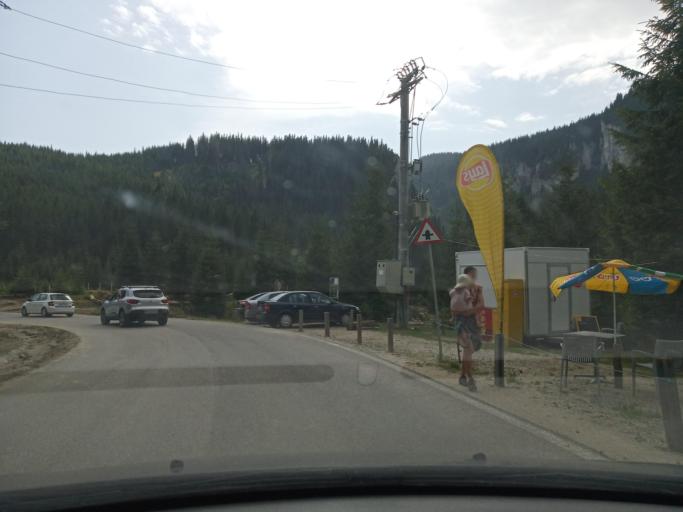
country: RO
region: Dambovita
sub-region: Comuna Moroeni
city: Glod
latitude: 45.3313
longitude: 25.4288
